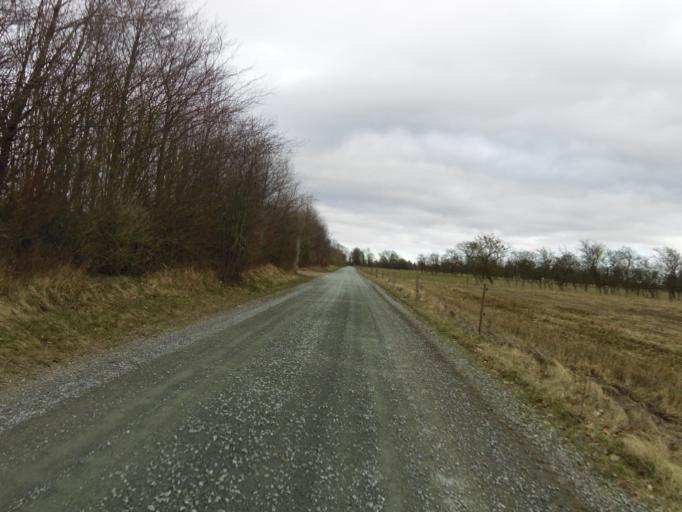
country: DK
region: South Denmark
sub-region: Tonder Kommune
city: Toftlund
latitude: 55.2123
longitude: 9.1685
